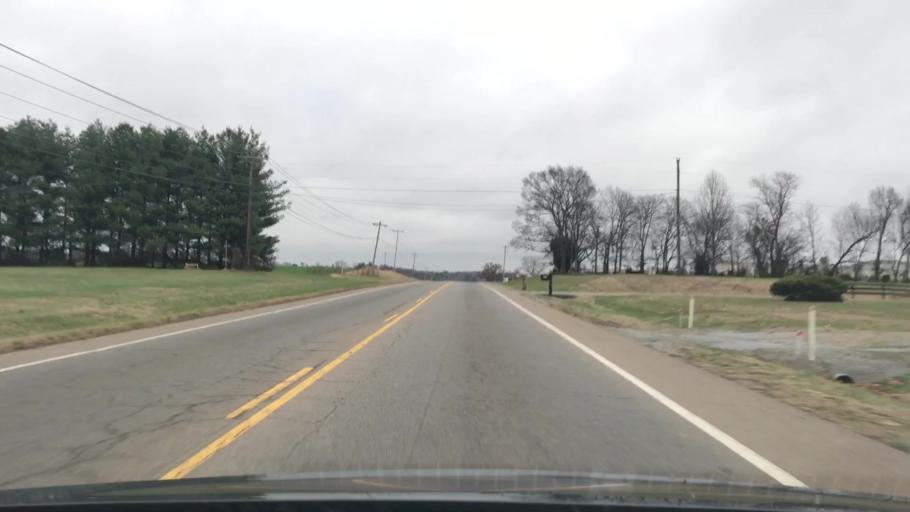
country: US
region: Kentucky
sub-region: Todd County
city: Guthrie
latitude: 36.6160
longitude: -87.2404
